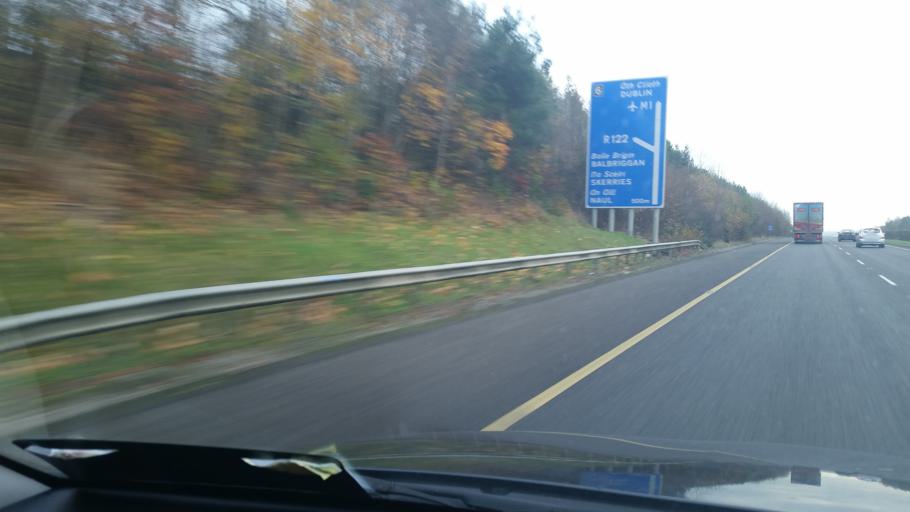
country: IE
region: Leinster
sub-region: An Mhi
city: Stamullin
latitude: 53.6077
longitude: -6.2328
